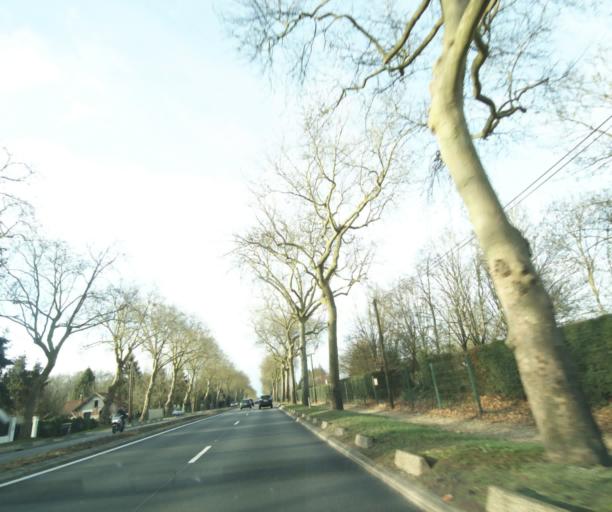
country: FR
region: Ile-de-France
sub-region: Departement des Yvelines
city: Louveciennes
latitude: 48.8505
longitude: 2.1085
